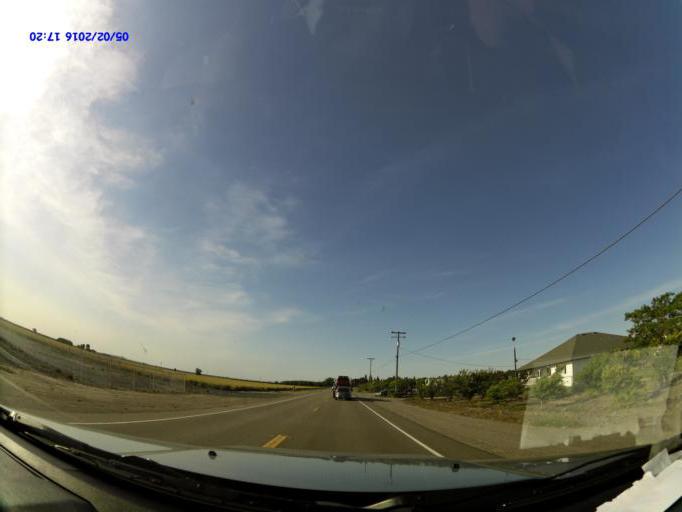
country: US
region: California
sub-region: San Joaquin County
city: Manteca
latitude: 37.8330
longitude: -121.1447
